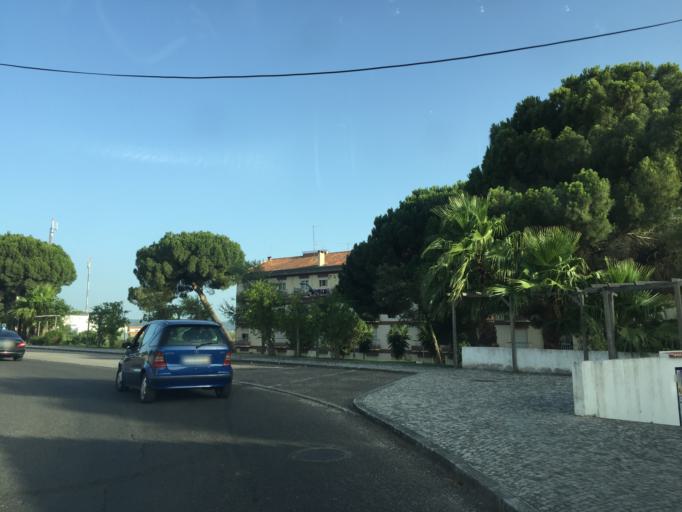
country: PT
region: Santarem
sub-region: Chamusca
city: Vila Nova da Barquinha
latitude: 39.4622
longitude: -8.4370
